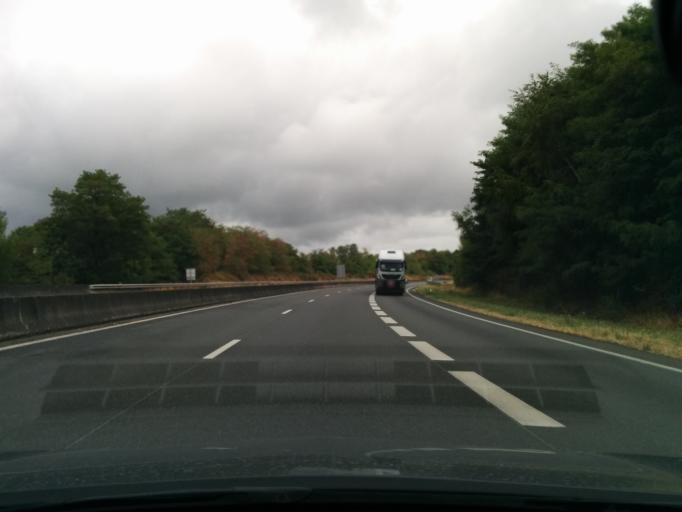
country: FR
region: Limousin
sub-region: Departement de la Correze
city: Donzenac
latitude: 45.2435
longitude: 1.5133
